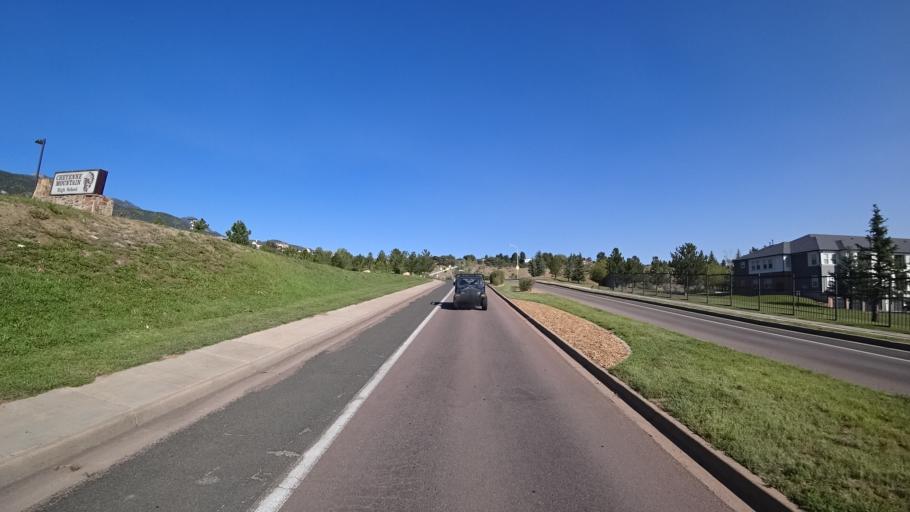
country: US
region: Colorado
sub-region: El Paso County
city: Colorado Springs
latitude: 38.8045
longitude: -104.8554
